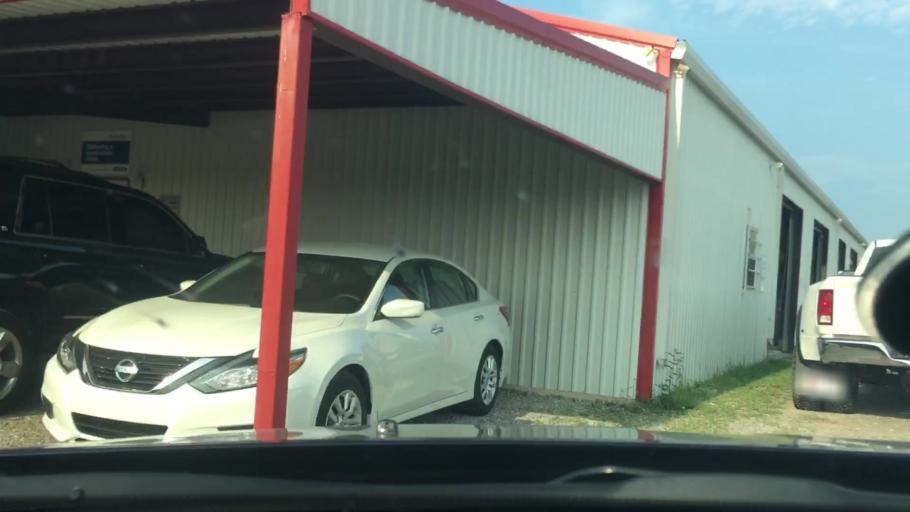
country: US
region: Oklahoma
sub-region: Bryan County
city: Durant
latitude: 34.0209
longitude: -96.3921
